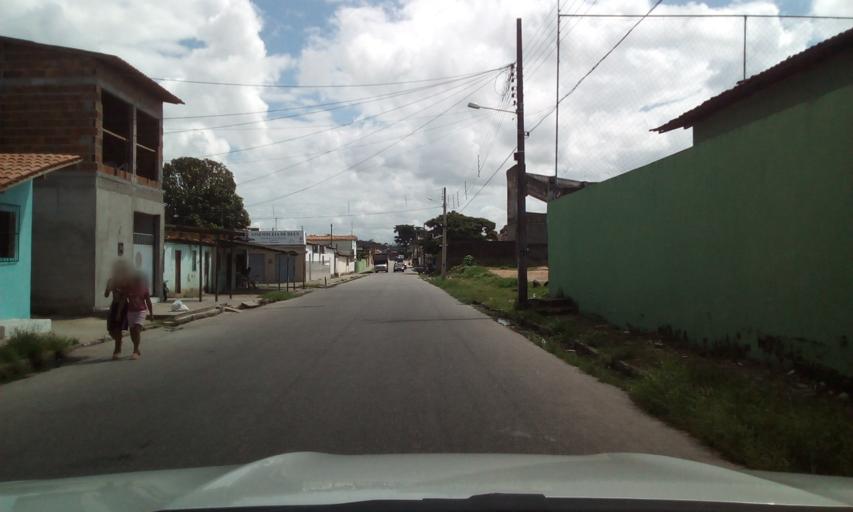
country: BR
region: Paraiba
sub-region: Bayeux
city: Bayeux
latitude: -7.1344
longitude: -34.9257
